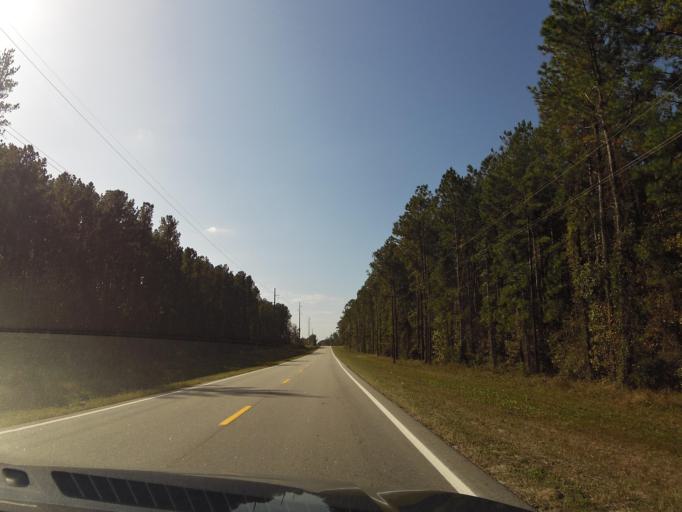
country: US
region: Georgia
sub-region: Charlton County
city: Folkston
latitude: 30.7672
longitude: -82.0641
